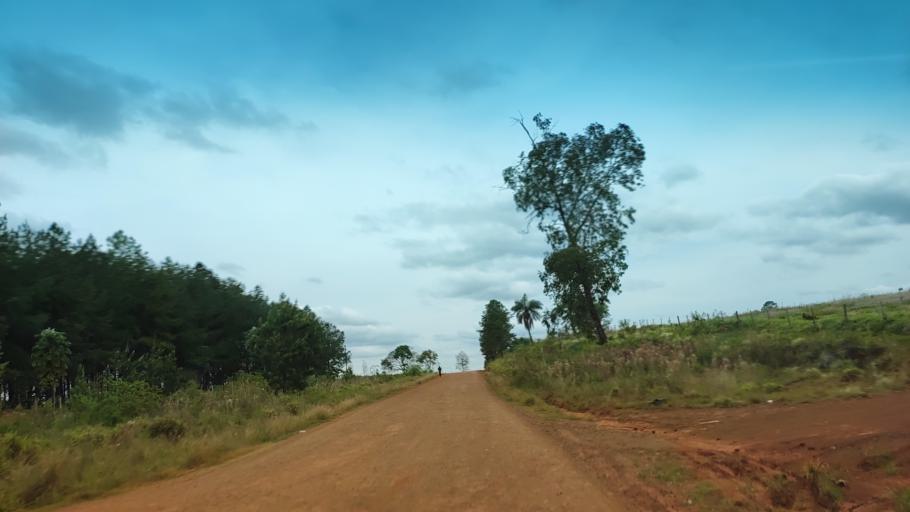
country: AR
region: Misiones
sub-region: Departamento de Capital
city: Posadas
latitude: -27.4815
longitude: -55.9708
